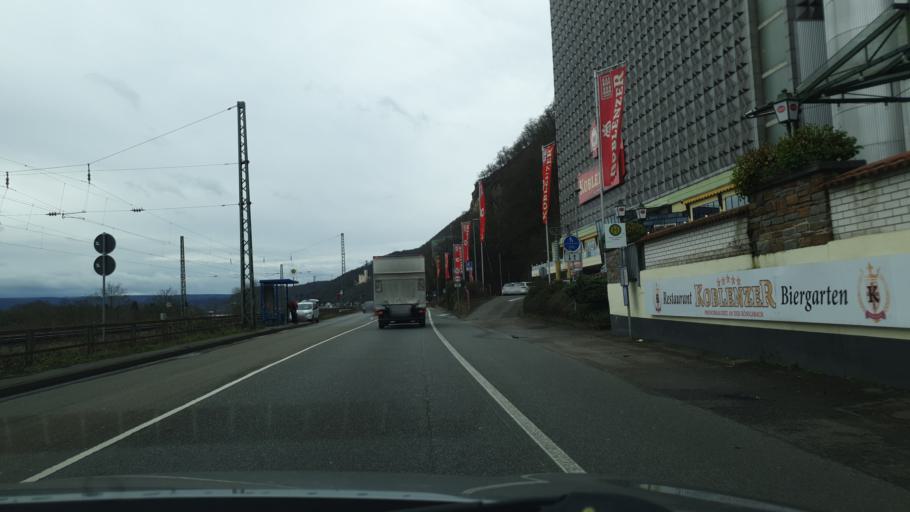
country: DE
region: Rheinland-Pfalz
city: Koblenz
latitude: 50.3217
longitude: 7.5862
